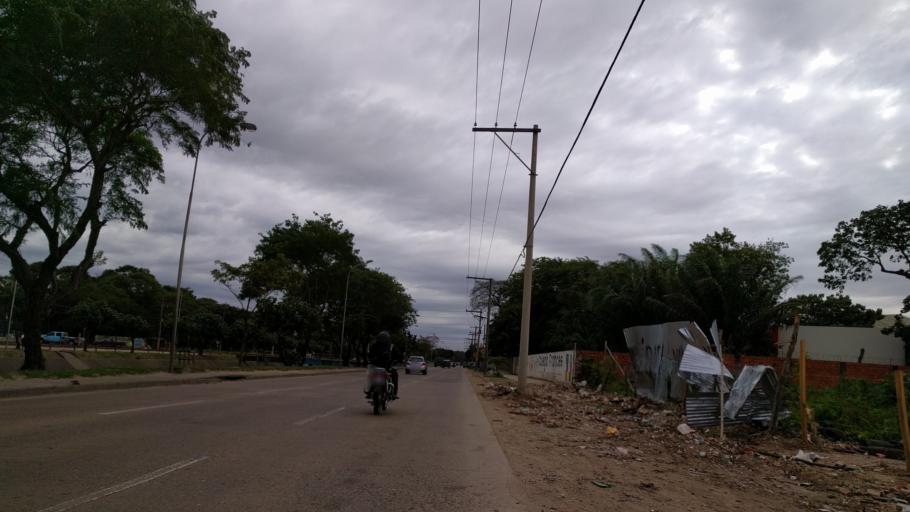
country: BO
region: Santa Cruz
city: Santa Cruz de la Sierra
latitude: -17.7845
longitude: -63.2164
